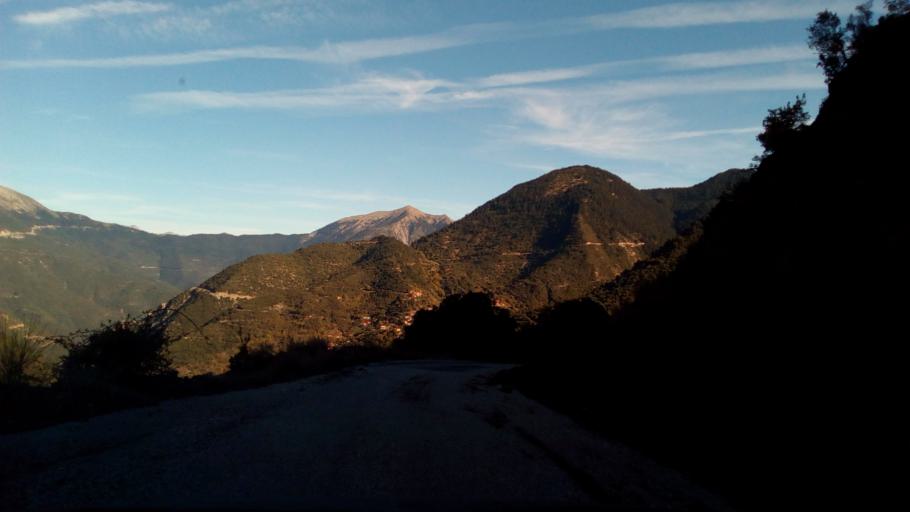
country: GR
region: West Greece
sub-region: Nomos Aitolias kai Akarnanias
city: Nafpaktos
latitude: 38.5501
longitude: 21.8529
